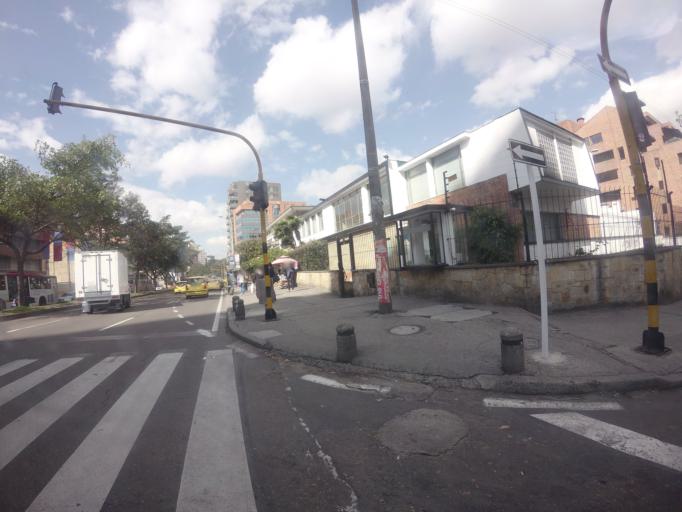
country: CO
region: Bogota D.C.
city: Barrio San Luis
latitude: 4.6631
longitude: -74.0490
